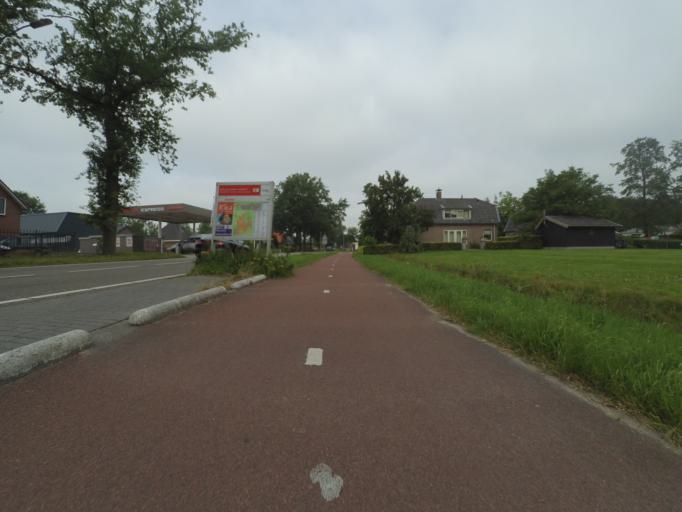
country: NL
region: Gelderland
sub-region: Gemeente Barneveld
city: Barneveld
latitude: 52.1325
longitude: 5.6054
